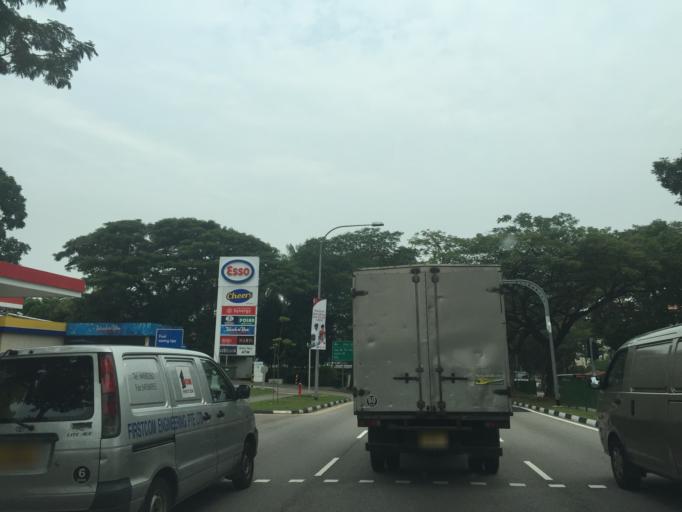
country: SG
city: Singapore
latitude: 1.3733
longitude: 103.8286
